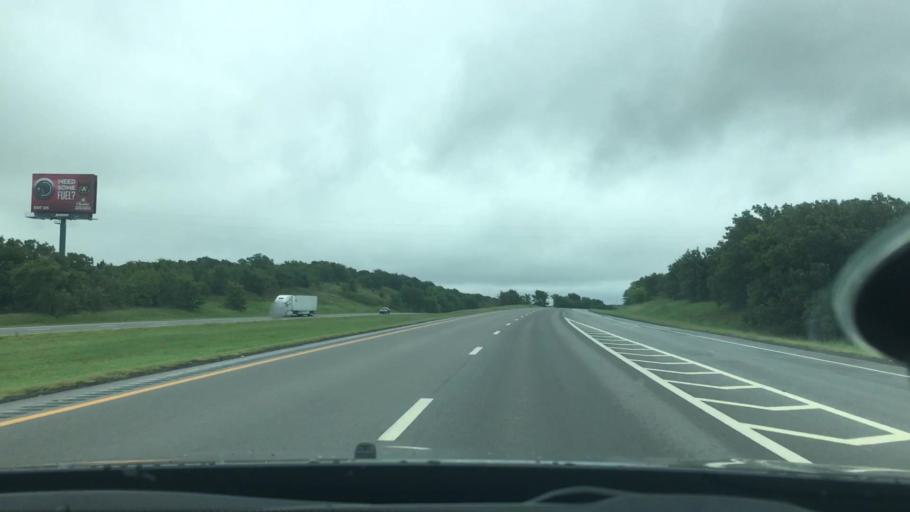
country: US
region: Oklahoma
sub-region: Okmulgee County
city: Henryetta
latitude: 35.4362
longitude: -95.8355
